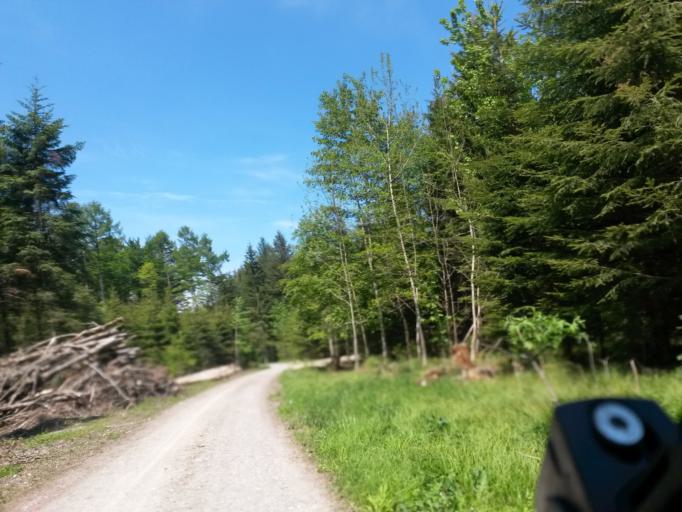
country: DE
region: Baden-Wuerttemberg
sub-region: Tuebingen Region
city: Bad Waldsee
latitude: 47.9440
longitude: 9.6986
